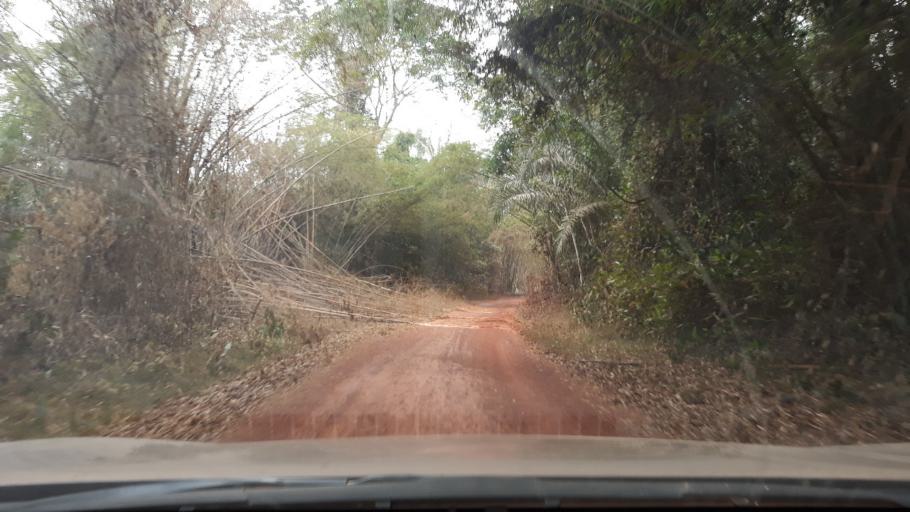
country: CD
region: Eastern Province
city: Buta
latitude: 2.2868
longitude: 25.0548
